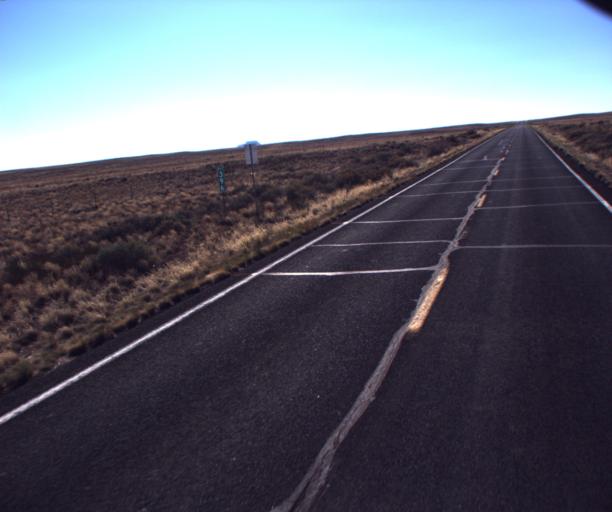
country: US
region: Arizona
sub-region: Navajo County
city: First Mesa
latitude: 35.6545
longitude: -110.4908
